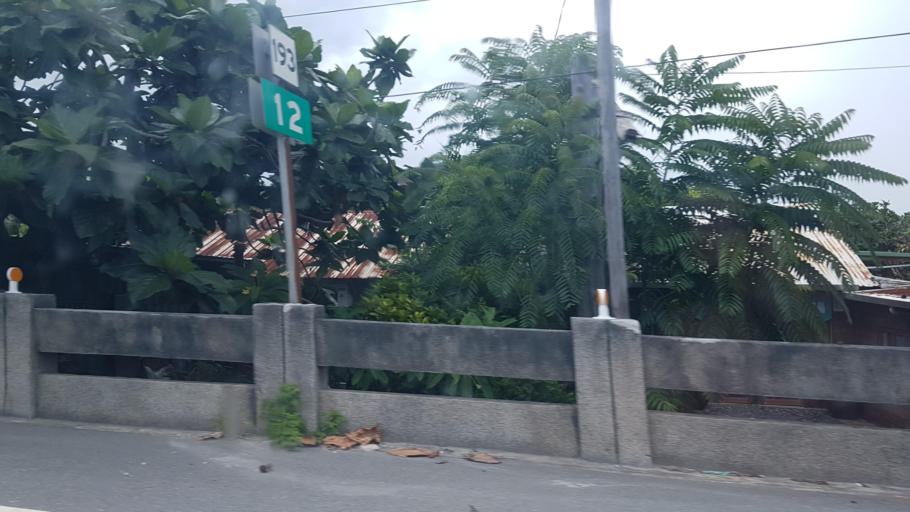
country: TW
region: Taiwan
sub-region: Hualien
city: Hualian
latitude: 24.0047
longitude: 121.6352
